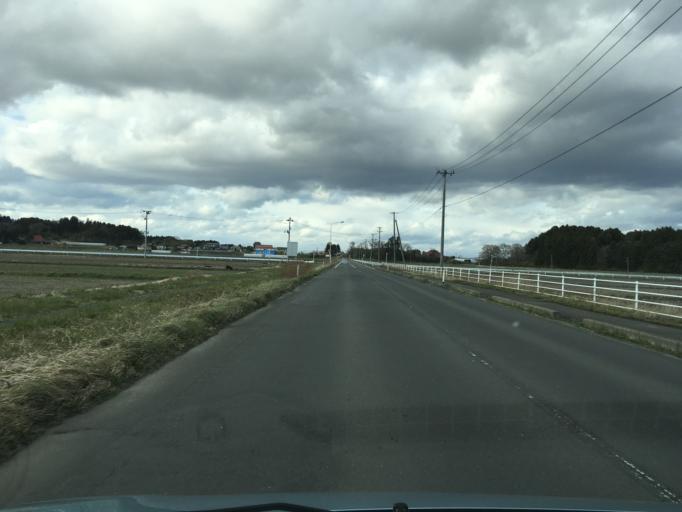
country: JP
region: Miyagi
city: Wakuya
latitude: 38.6468
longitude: 141.1899
